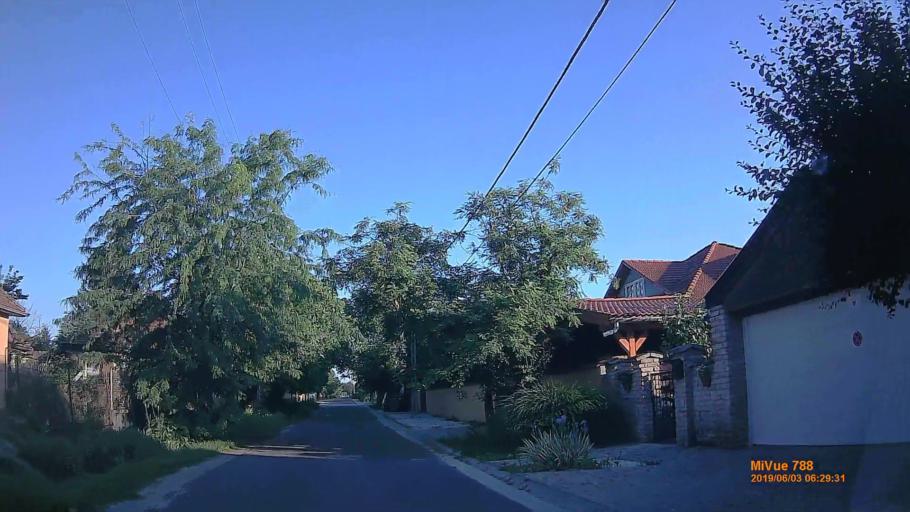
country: HU
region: Pest
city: Dunavarsany
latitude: 47.2745
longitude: 19.0699
